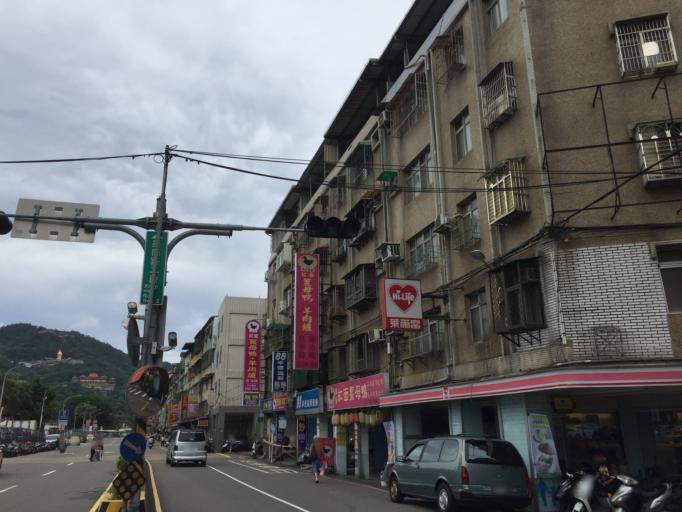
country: TW
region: Taipei
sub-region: Taipei
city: Banqiao
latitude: 24.9840
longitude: 121.5048
